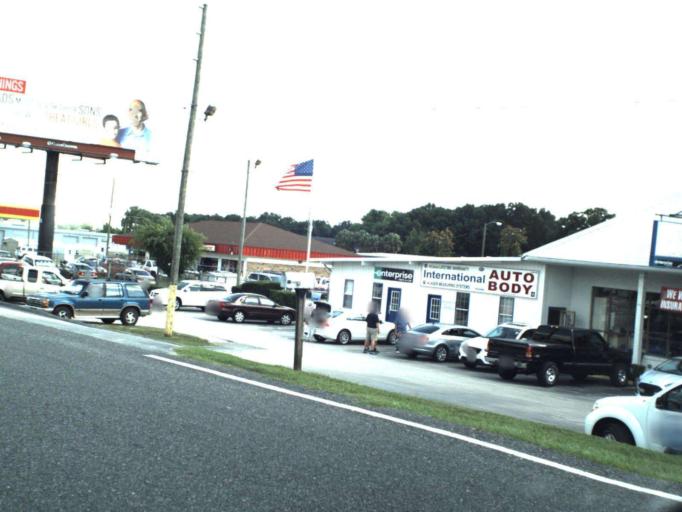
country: US
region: Florida
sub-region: Marion County
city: Silver Springs Shores
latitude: 29.1493
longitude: -82.0735
